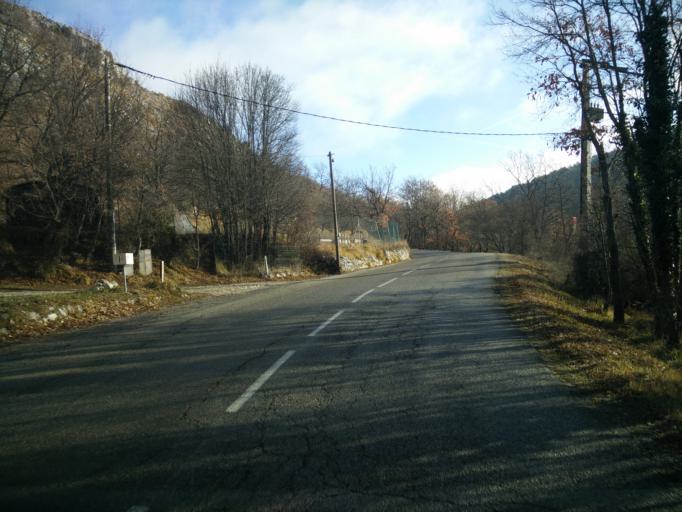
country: FR
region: Provence-Alpes-Cote d'Azur
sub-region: Departement des Alpes-Maritimes
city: Tourrettes-sur-Loup
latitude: 43.7863
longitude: 7.0162
